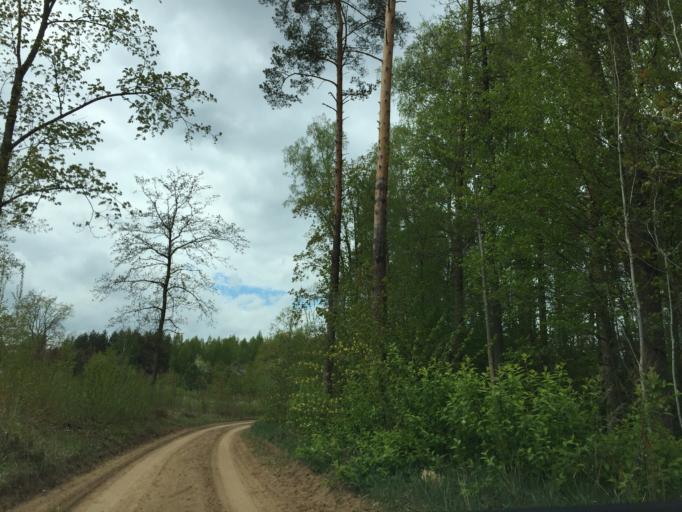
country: LV
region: Kekava
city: Kekava
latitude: 56.8015
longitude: 24.3000
